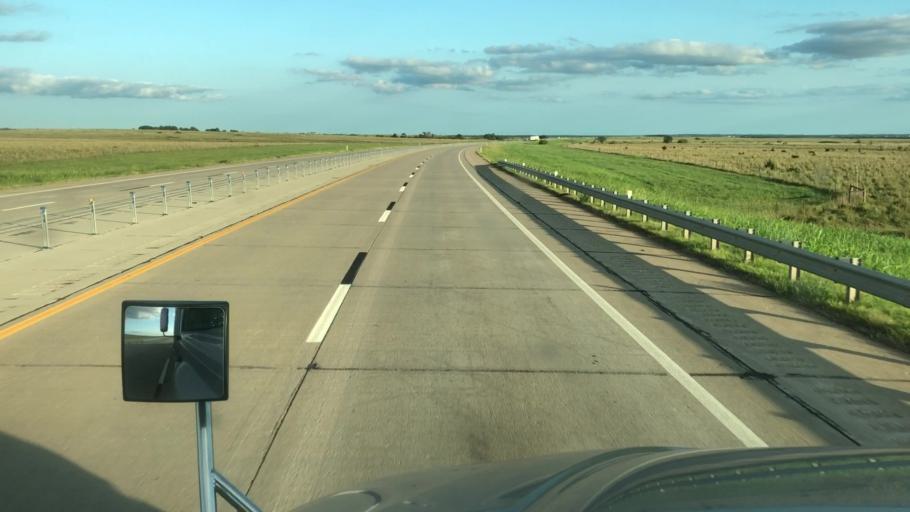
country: US
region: Oklahoma
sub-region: Pawnee County
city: Pawnee
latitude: 36.3703
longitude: -97.0372
